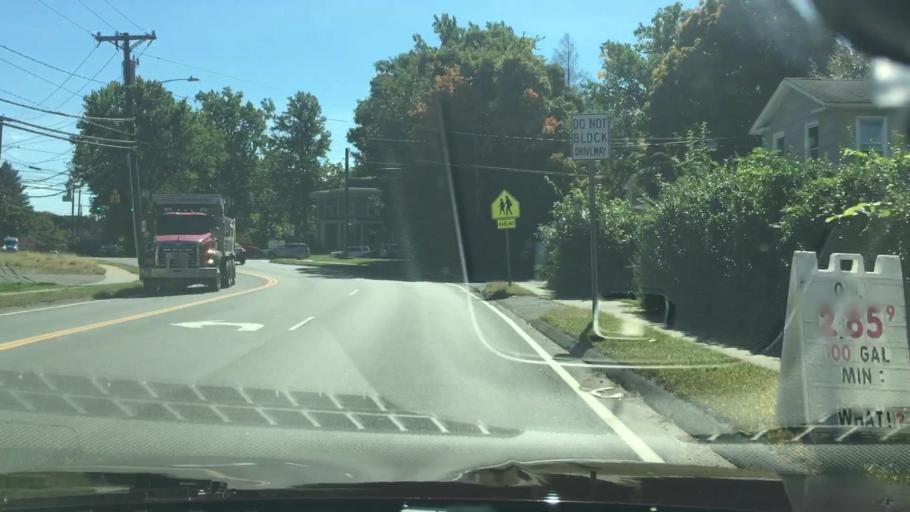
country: US
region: Connecticut
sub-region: Hartford County
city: Plainville
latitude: 41.6778
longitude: -72.9033
